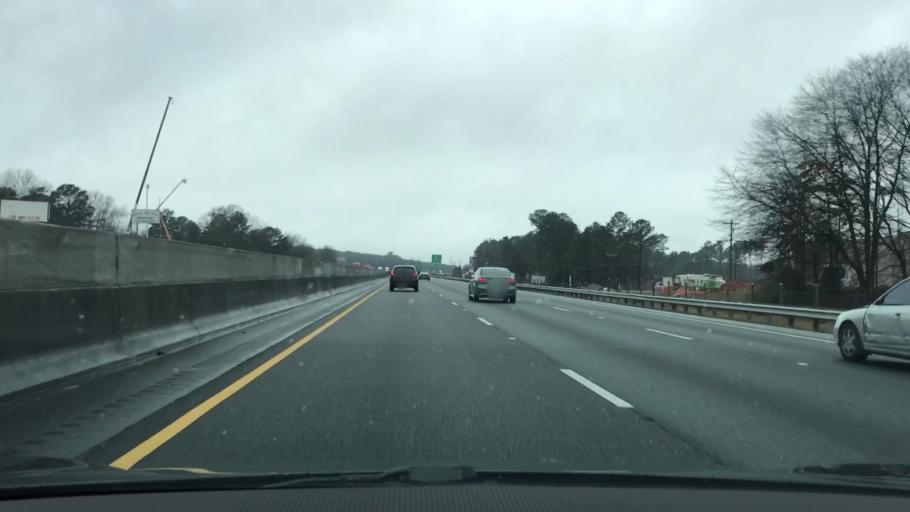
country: US
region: Georgia
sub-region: Rockdale County
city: Conyers
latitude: 33.6308
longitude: -83.9632
